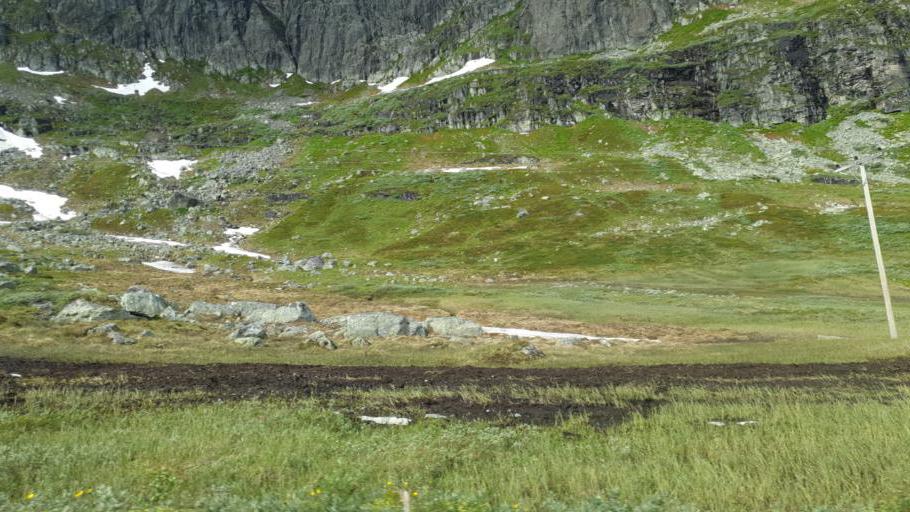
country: NO
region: Oppland
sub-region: Vestre Slidre
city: Slidre
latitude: 61.3013
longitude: 8.8080
